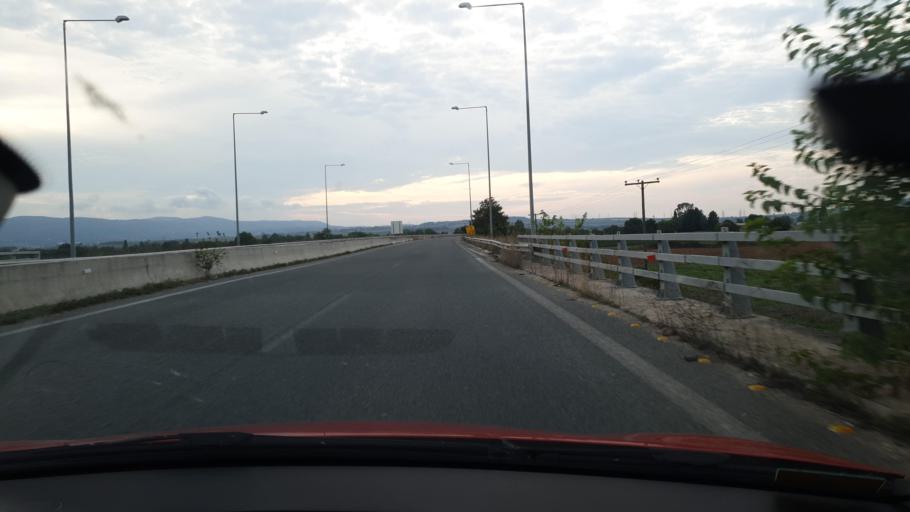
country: GR
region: Central Macedonia
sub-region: Nomos Thessalonikis
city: Assiros
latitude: 40.7833
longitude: 23.0194
